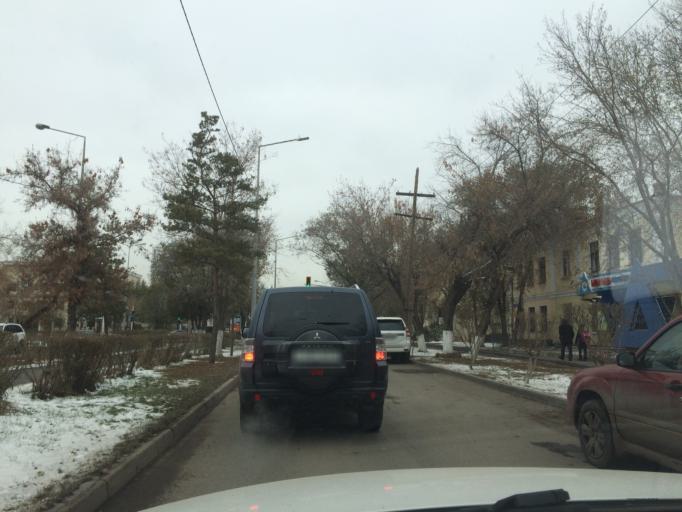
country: KZ
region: Astana Qalasy
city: Astana
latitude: 51.1631
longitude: 71.4150
